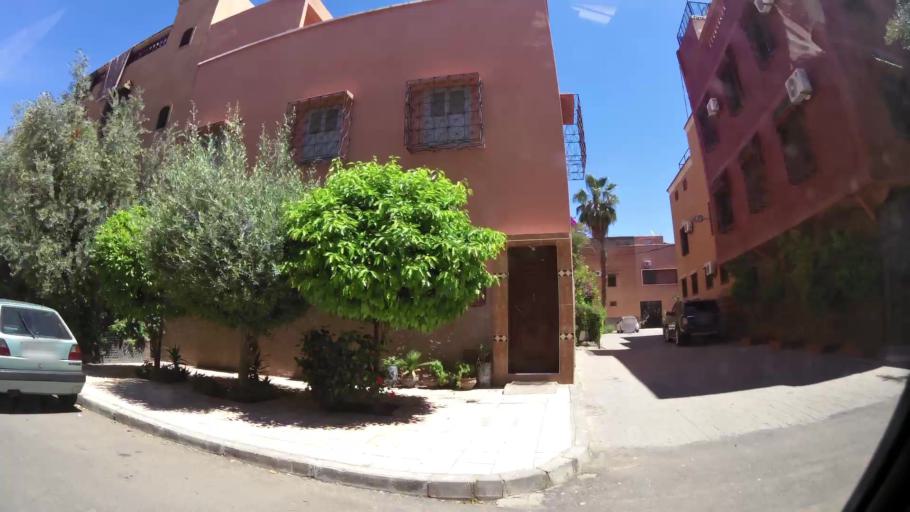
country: MA
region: Marrakech-Tensift-Al Haouz
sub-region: Marrakech
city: Marrakesh
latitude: 31.6480
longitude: -7.9942
